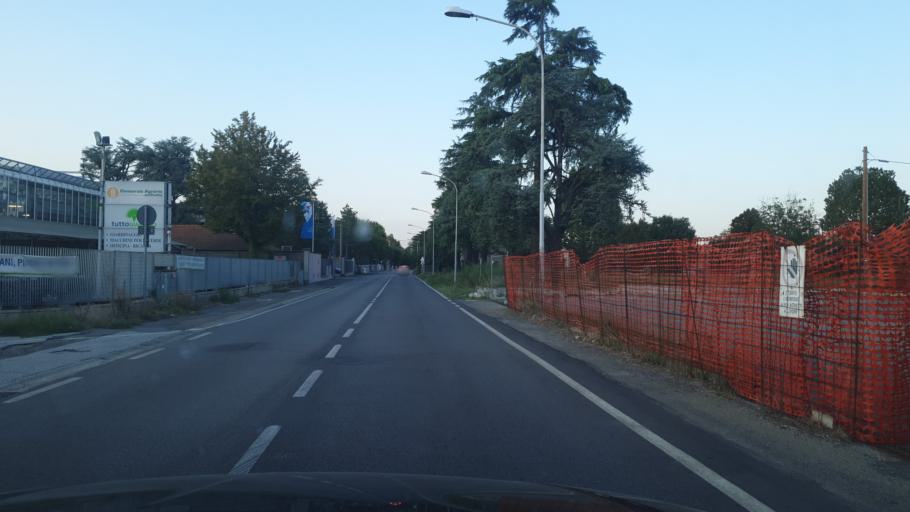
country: IT
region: Emilia-Romagna
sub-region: Provincia di Bologna
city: Quarto Inferiore
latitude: 44.5459
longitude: 11.3971
